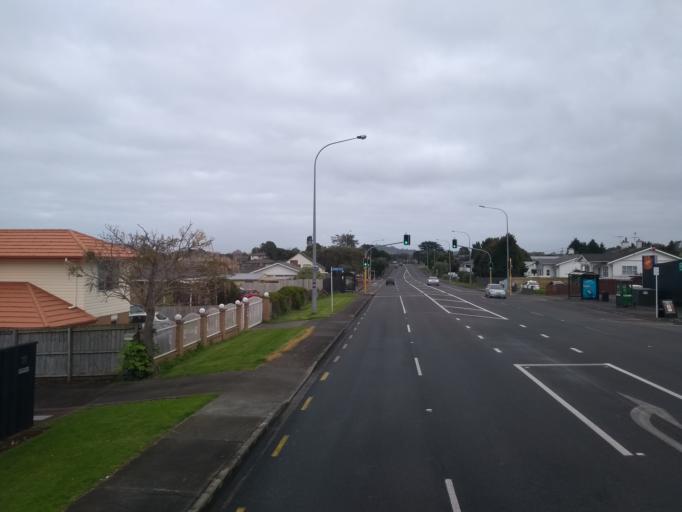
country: NZ
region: Auckland
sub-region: Auckland
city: Tamaki
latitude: -36.8968
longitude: 174.8327
